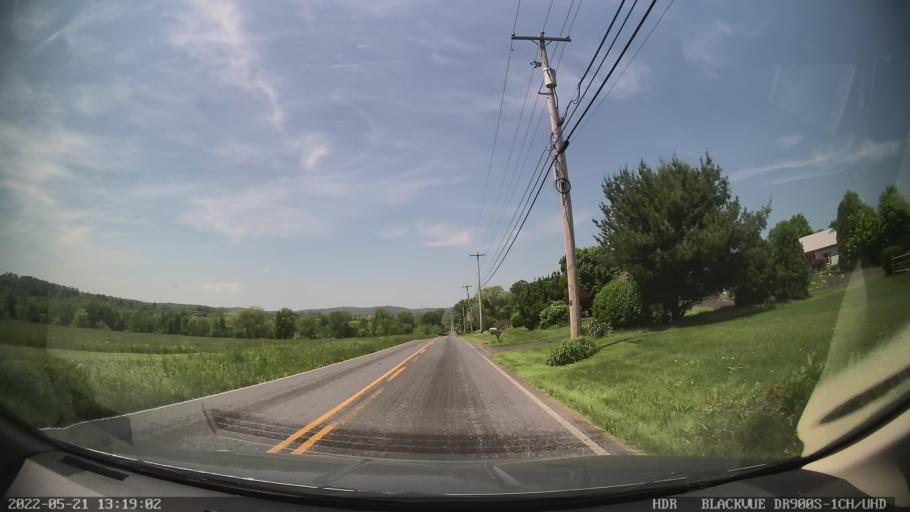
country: US
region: Pennsylvania
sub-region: Berks County
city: Bally
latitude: 40.3710
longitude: -75.5989
